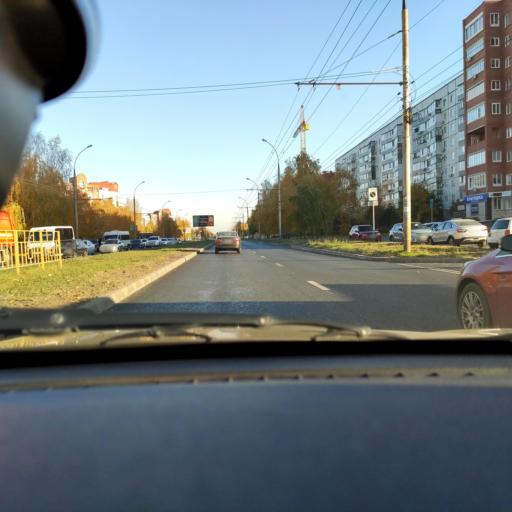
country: RU
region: Samara
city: Tol'yatti
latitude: 53.5263
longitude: 49.3269
